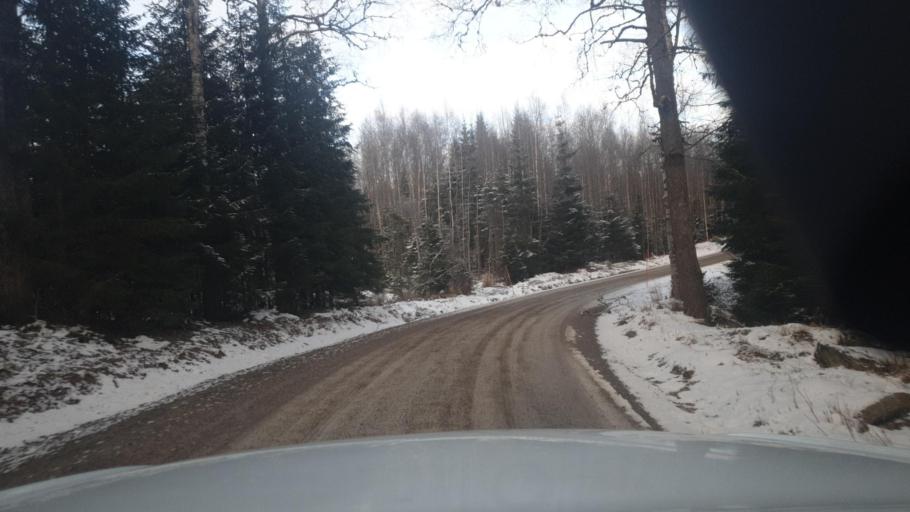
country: SE
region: Vaermland
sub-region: Arvika Kommun
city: Arvika
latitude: 59.9529
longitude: 12.6590
